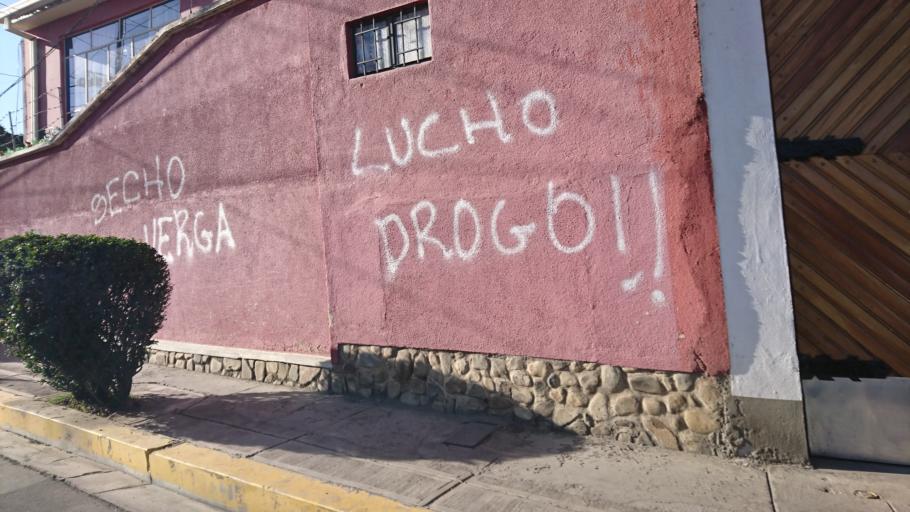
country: BO
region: La Paz
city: La Paz
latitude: -16.5256
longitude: -68.1020
